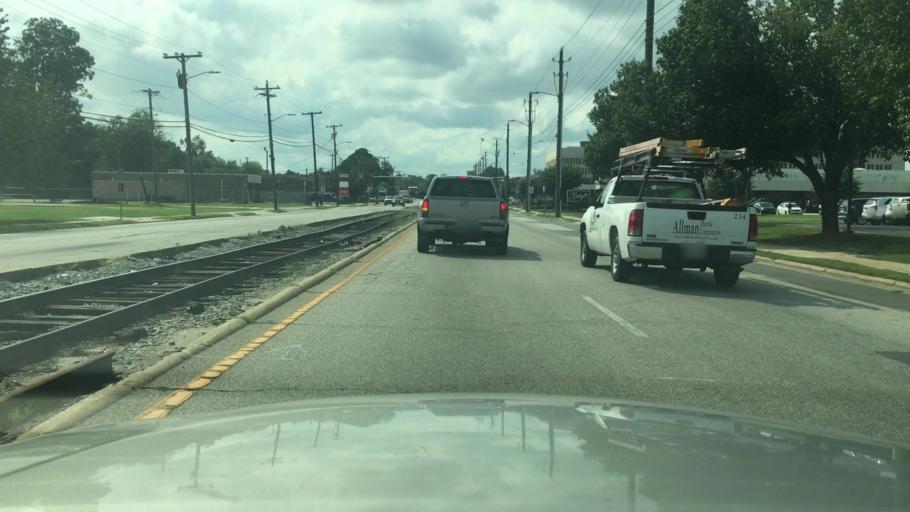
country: US
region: North Carolina
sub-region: Cumberland County
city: Fayetteville
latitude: 35.0486
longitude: -78.8732
